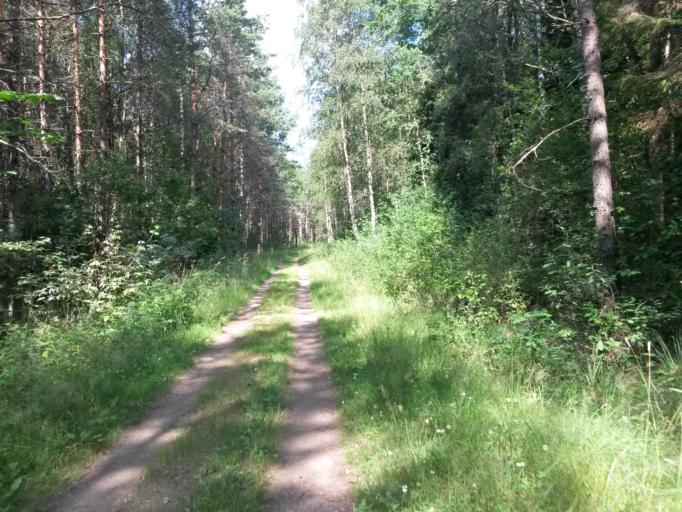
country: SE
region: Vaestra Goetaland
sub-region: Vargarda Kommun
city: Vargarda
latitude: 58.0382
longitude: 12.8305
